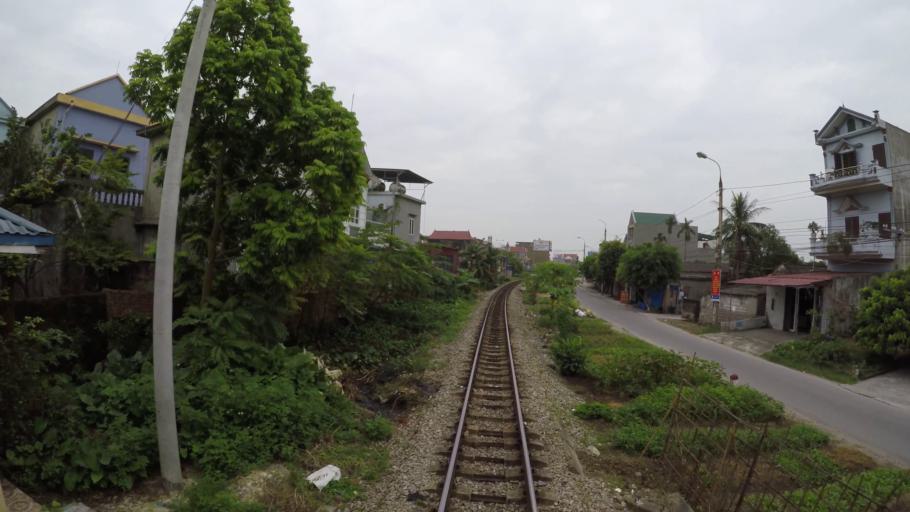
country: VN
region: Hai Duong
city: Phu Thai
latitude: 20.9680
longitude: 106.5031
